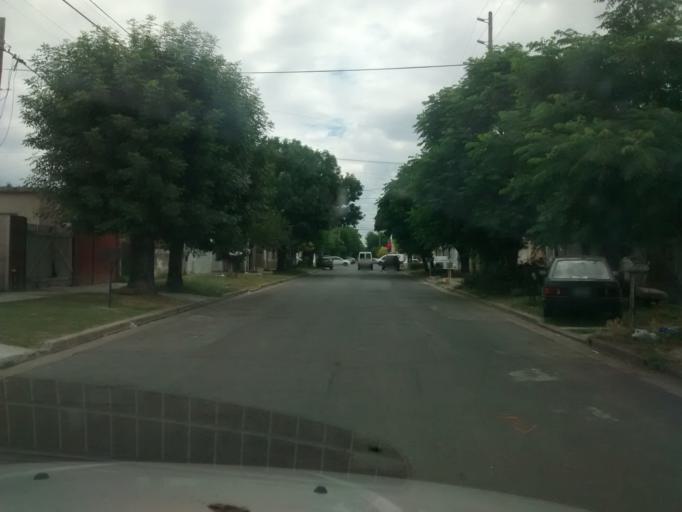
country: AR
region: Buenos Aires
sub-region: Partido de La Plata
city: La Plata
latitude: -34.9264
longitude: -57.9187
